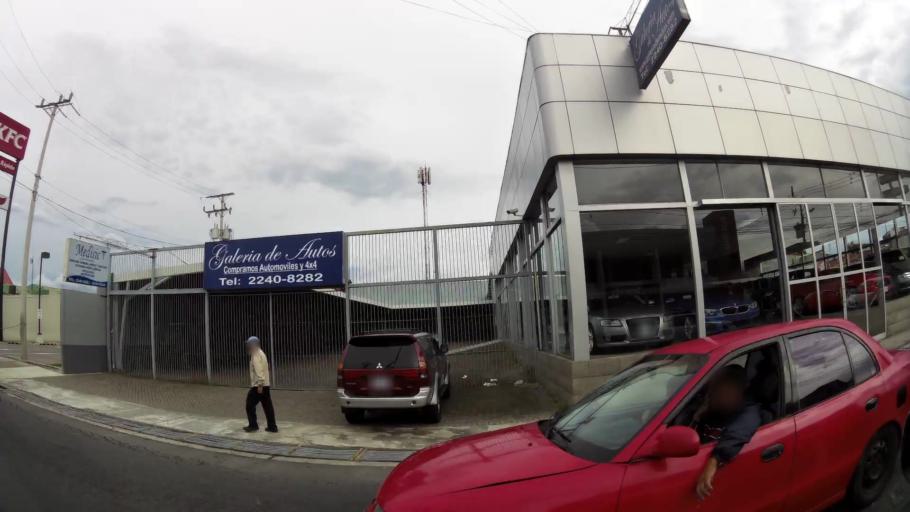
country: CR
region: San Jose
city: San Juan
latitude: 9.9623
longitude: -84.0768
